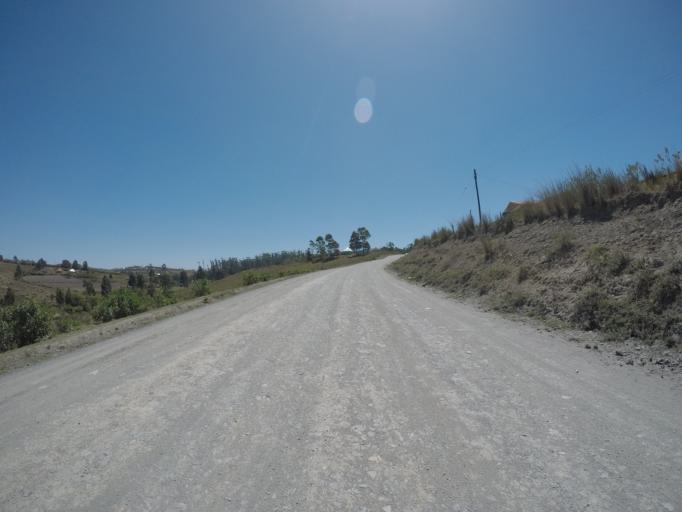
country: ZA
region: Eastern Cape
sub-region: OR Tambo District Municipality
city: Libode
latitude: -31.9655
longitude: 29.0252
